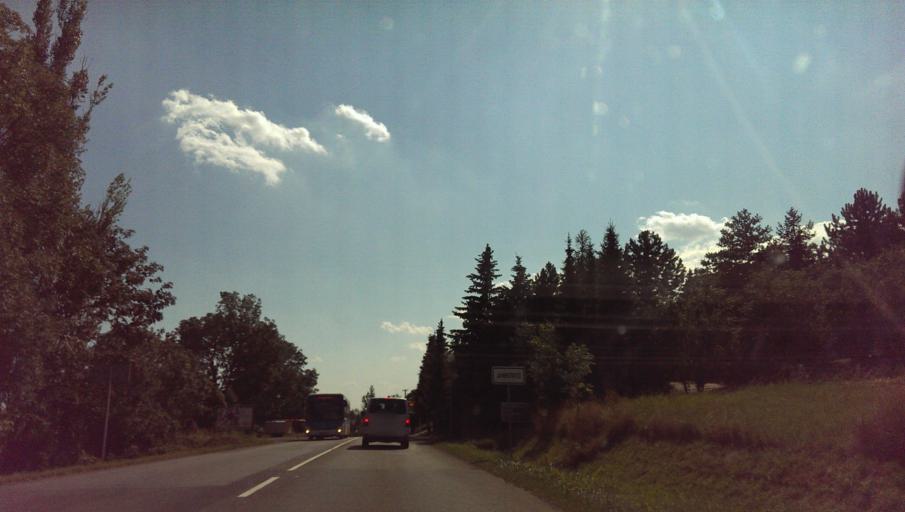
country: CZ
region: Zlin
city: Prusinovice
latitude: 49.3592
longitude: 17.6155
